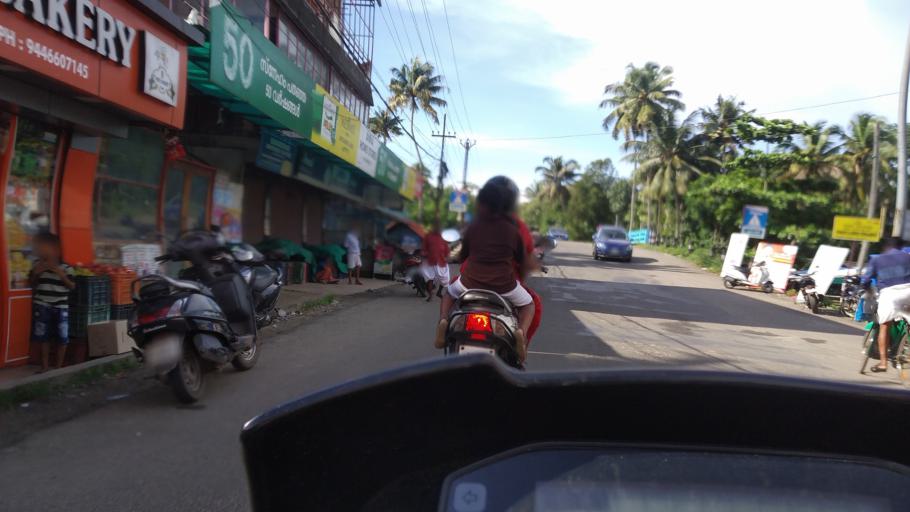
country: IN
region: Kerala
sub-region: Ernakulam
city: Elur
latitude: 10.0665
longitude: 76.2129
